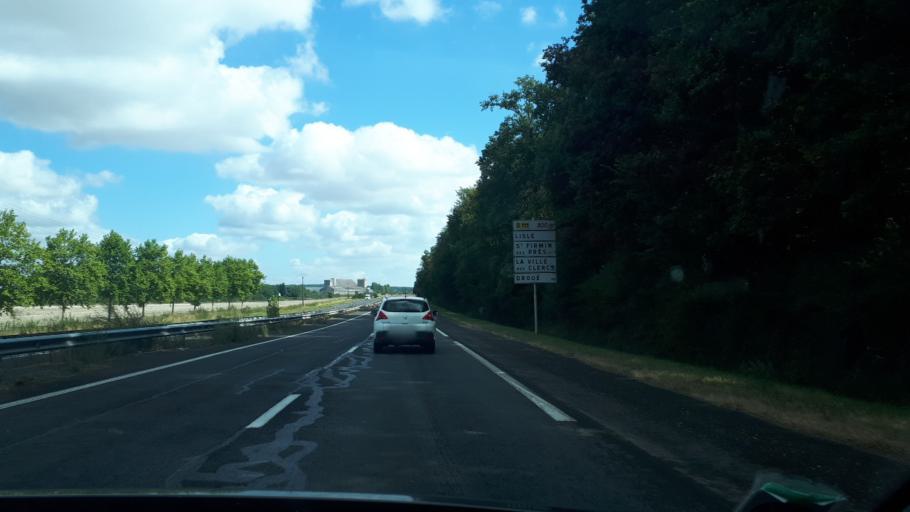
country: FR
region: Centre
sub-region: Departement du Loir-et-Cher
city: Saint-Ouen
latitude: 47.8376
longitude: 1.0879
